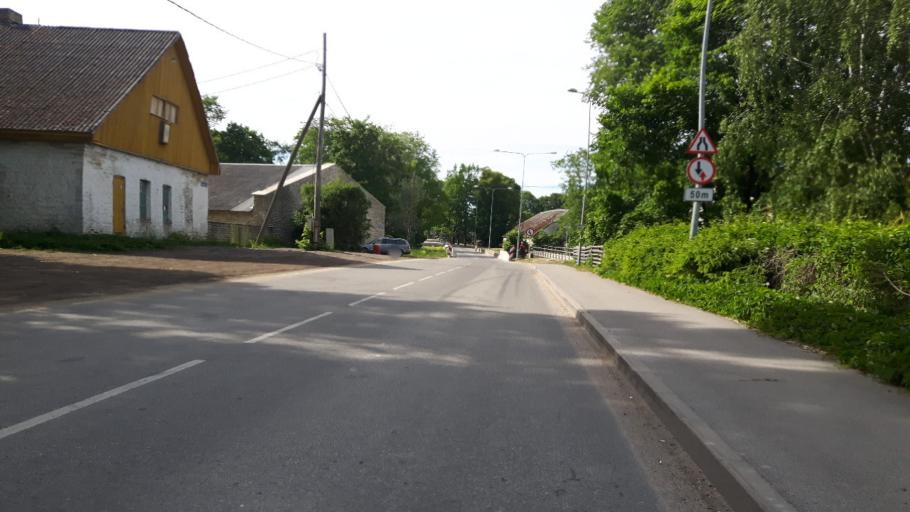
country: EE
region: Harju
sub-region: Raasiku vald
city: Arukula
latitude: 59.4264
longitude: 25.0990
